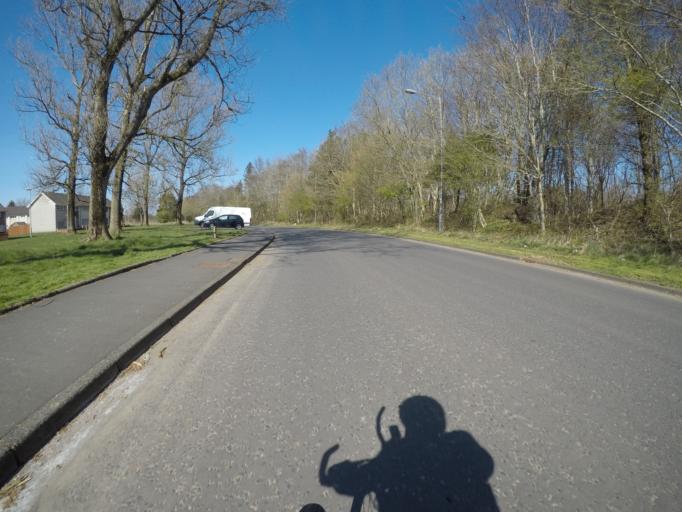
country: GB
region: Scotland
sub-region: North Ayrshire
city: Irvine
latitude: 55.6352
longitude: -4.6613
